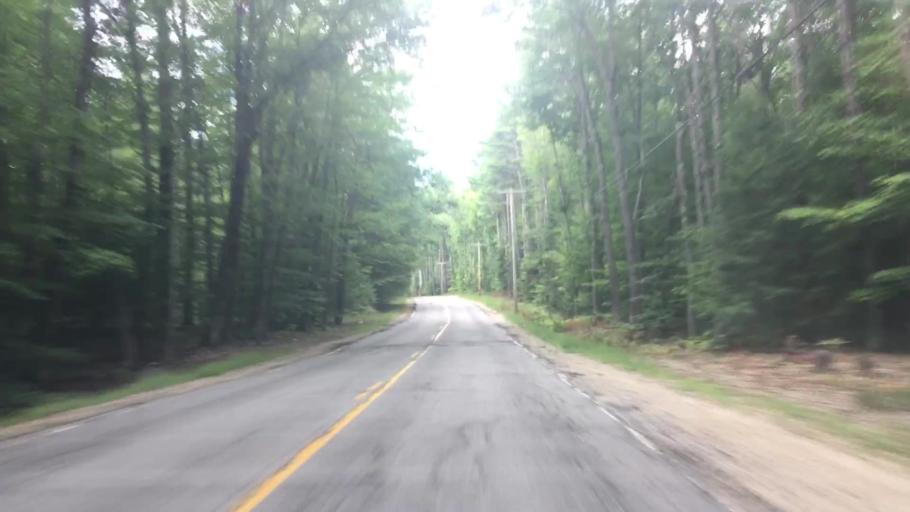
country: US
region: Maine
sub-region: Oxford County
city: Oxford
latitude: 44.0322
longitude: -70.5327
